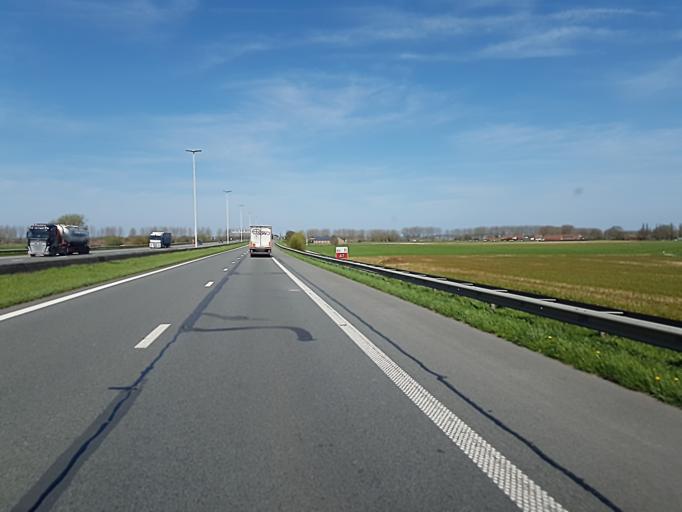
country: BE
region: Wallonia
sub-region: Province du Hainaut
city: Estaimpuis
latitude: 50.6930
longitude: 3.2935
